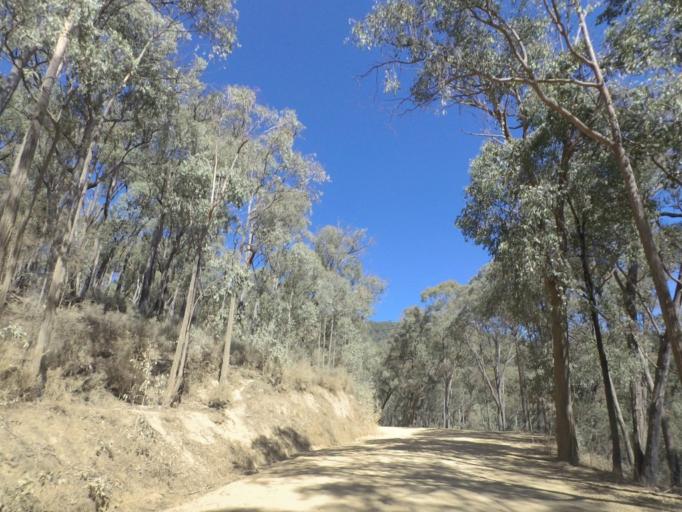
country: AU
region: Victoria
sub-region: Murrindindi
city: Alexandra
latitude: -37.3198
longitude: 145.8101
